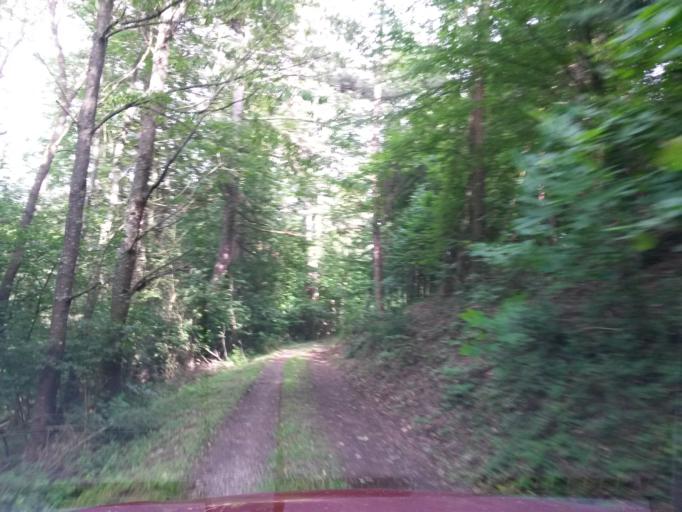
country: SK
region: Banskobystricky
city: Detva
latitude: 48.4179
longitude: 19.3564
